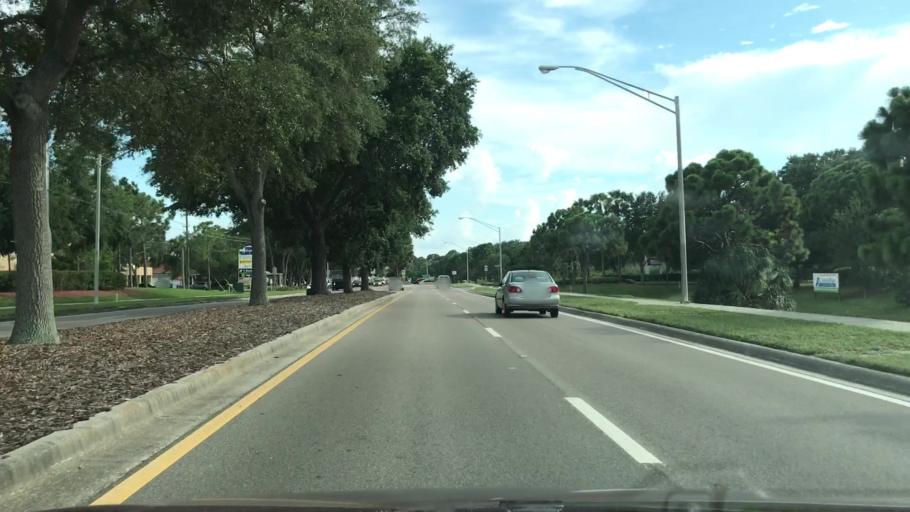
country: US
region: Florida
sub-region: Sarasota County
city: Venice Gardens
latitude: 27.0527
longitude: -82.3965
